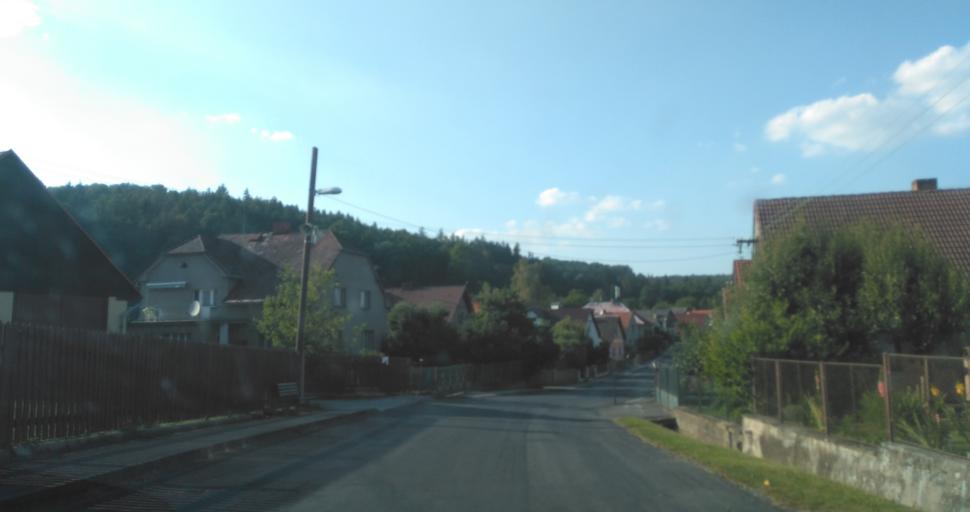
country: CZ
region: Central Bohemia
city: Roztoky
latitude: 49.9856
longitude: 13.8637
